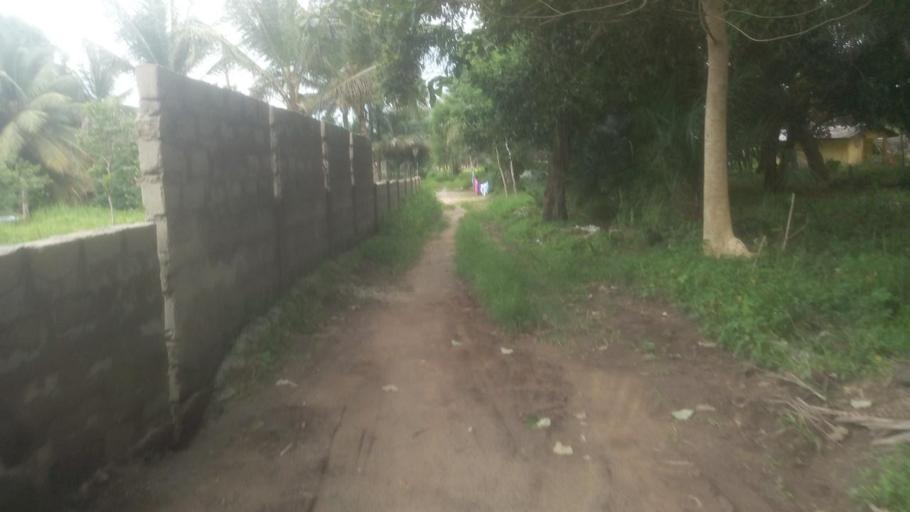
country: SL
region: Northern Province
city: Masoyila
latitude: 8.5627
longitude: -13.1654
